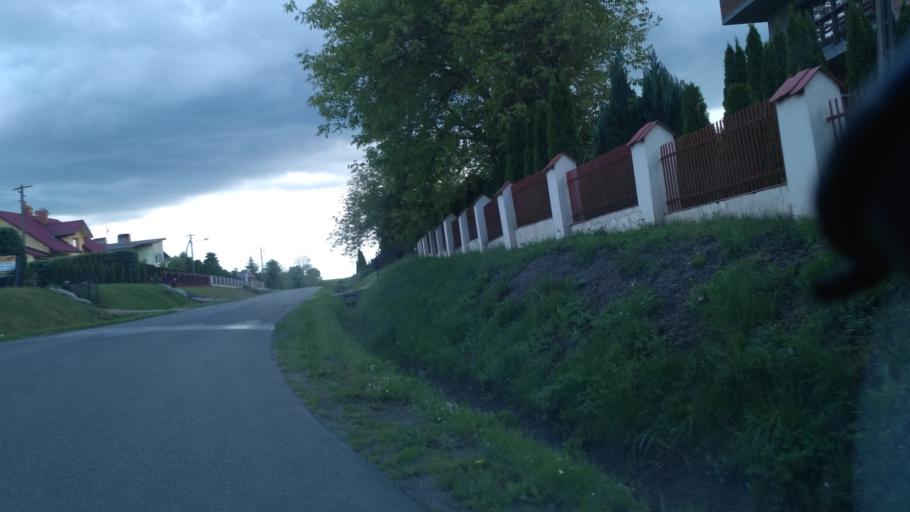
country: PL
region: Subcarpathian Voivodeship
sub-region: Powiat jaroslawski
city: Rokietnica
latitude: 49.9389
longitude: 22.6666
